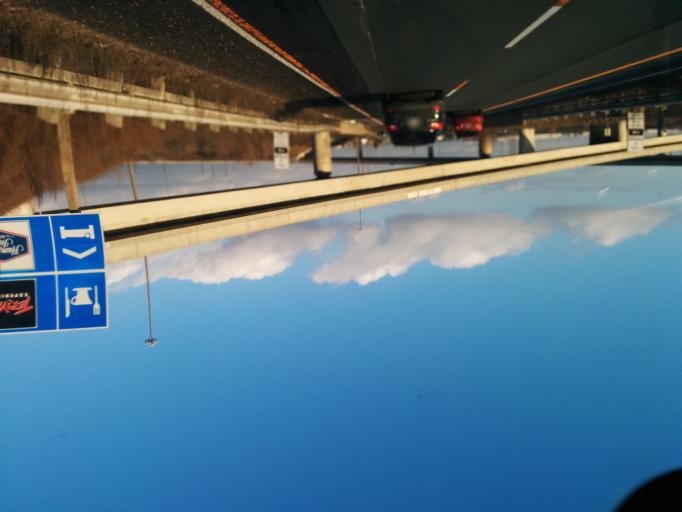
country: CA
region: Ontario
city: Etobicoke
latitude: 43.7527
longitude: -79.6310
